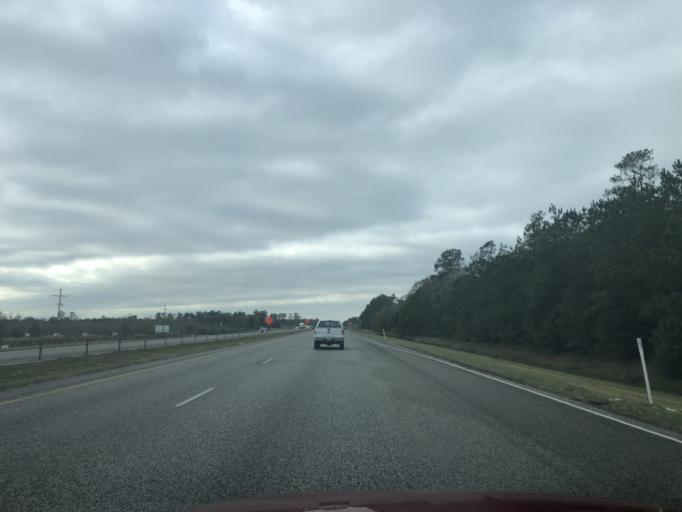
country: US
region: Texas
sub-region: Jefferson County
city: Fannett
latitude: 29.9272
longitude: -94.2743
